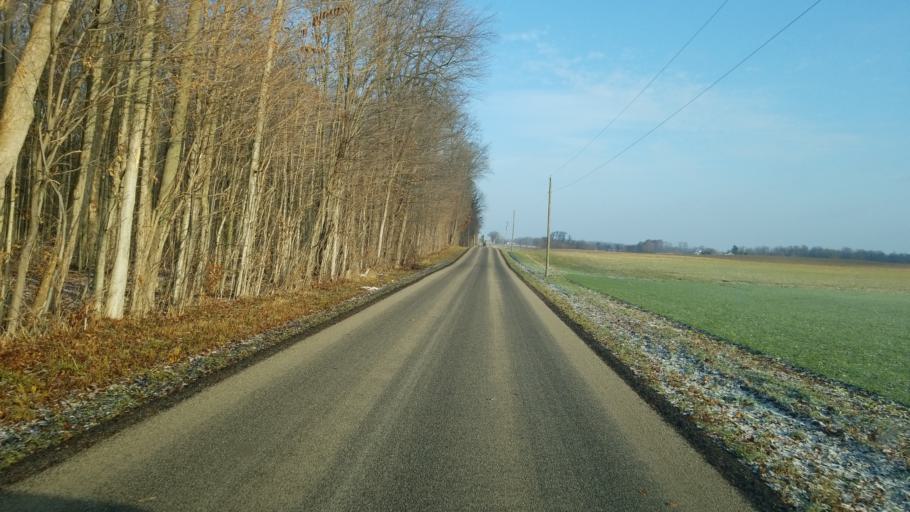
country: US
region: Ohio
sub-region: Crawford County
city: Crestline
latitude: 40.8603
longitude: -82.8275
